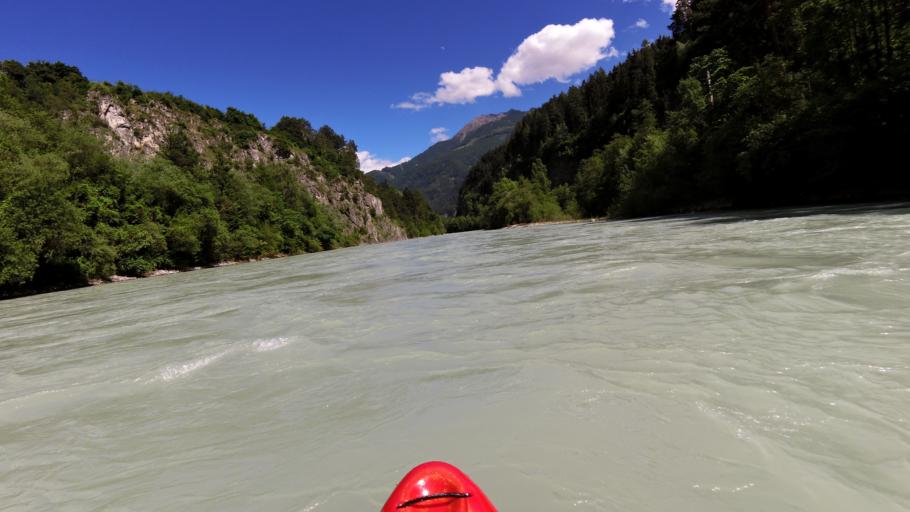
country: AT
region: Tyrol
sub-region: Politischer Bezirk Imst
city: Karrosten
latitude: 47.2188
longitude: 10.7661
